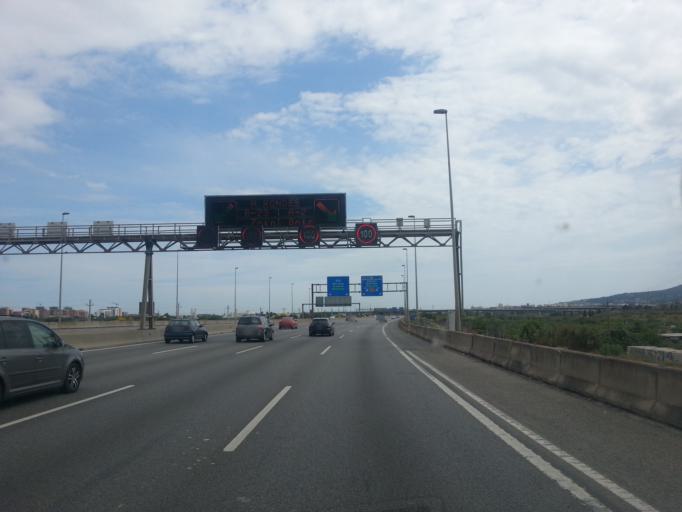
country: ES
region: Catalonia
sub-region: Provincia de Barcelona
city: Sant Vicenc dels Horts
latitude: 41.3884
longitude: 2.0267
